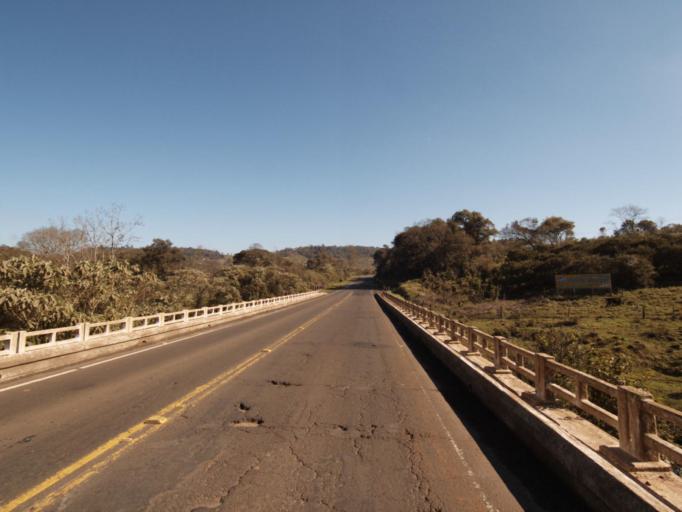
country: BR
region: Rio Grande do Sul
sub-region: Frederico Westphalen
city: Frederico Westphalen
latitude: -27.0788
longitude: -53.2264
